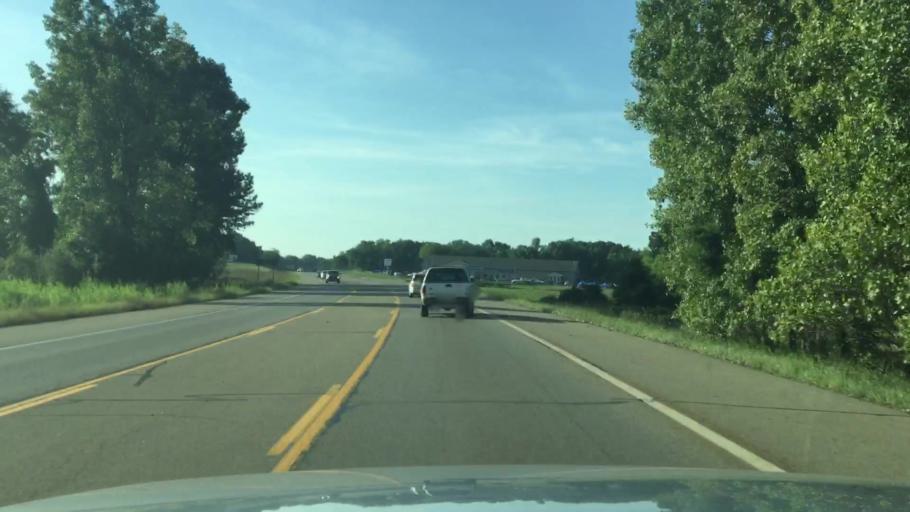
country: US
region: Michigan
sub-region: Jackson County
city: Vandercook Lake
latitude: 42.1872
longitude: -84.3692
